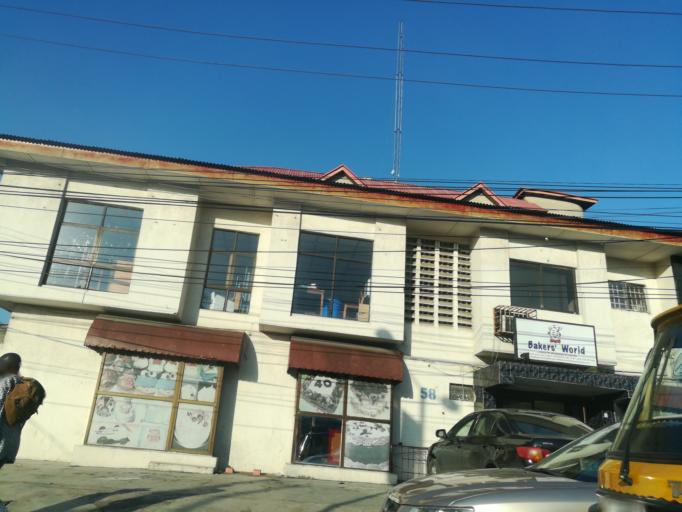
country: NG
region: Lagos
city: Ikeja
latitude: 6.6016
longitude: 3.3521
